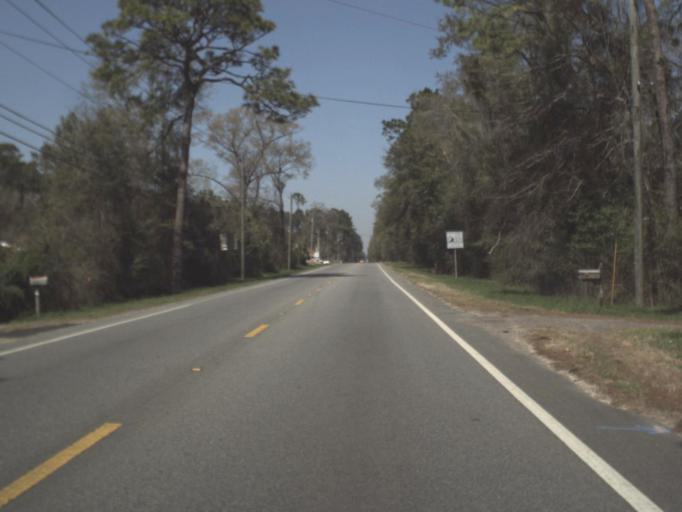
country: US
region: Florida
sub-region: Leon County
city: Woodville
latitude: 30.2921
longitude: -84.2428
